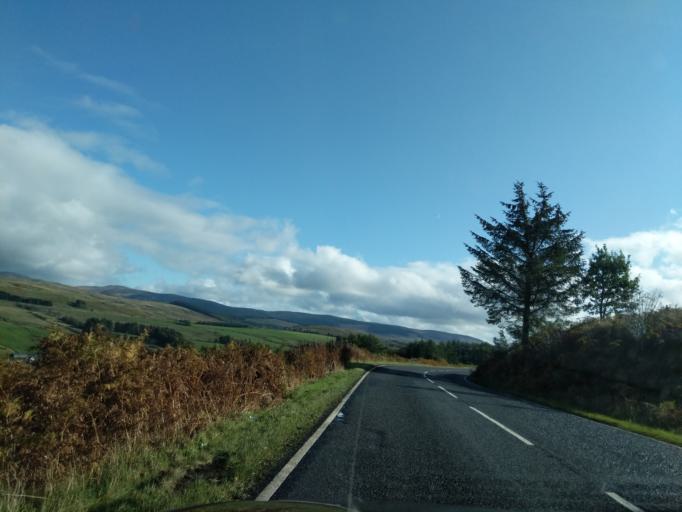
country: GB
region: Scotland
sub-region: Dumfries and Galloway
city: Moffat
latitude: 55.3587
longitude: -3.4738
